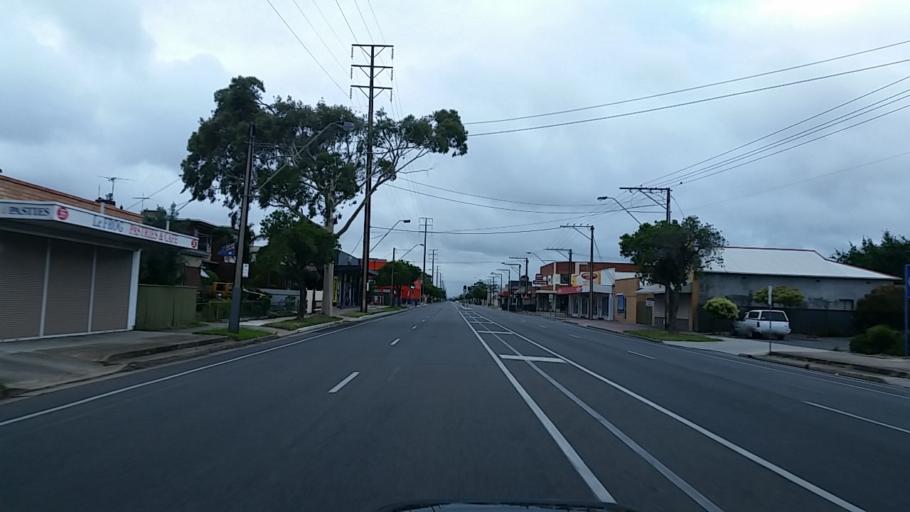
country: AU
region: South Australia
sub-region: Port Adelaide Enfield
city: Cheltenham
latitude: -34.8683
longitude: 138.5121
